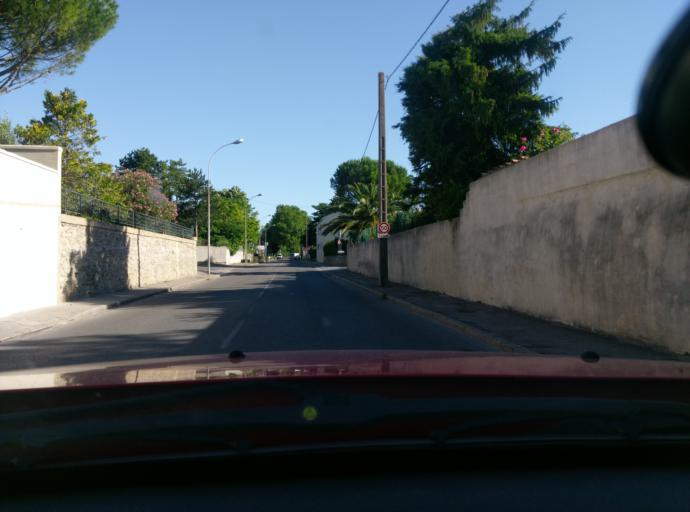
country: FR
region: Languedoc-Roussillon
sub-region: Departement du Gard
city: Uzes
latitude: 44.0179
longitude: 4.4163
